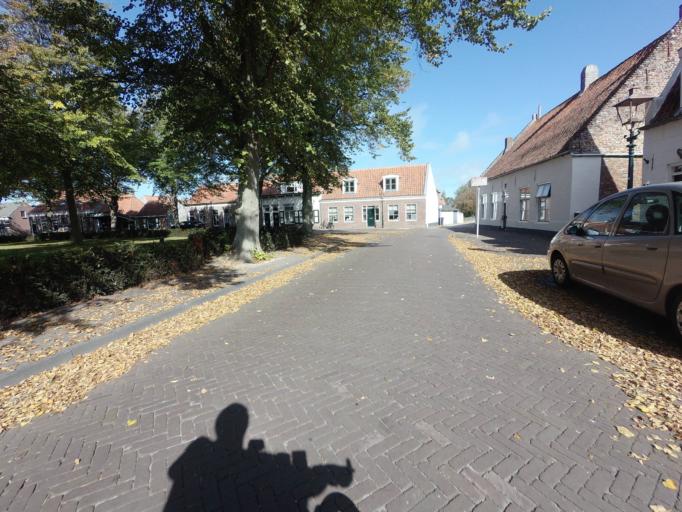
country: NL
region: Zeeland
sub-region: Gemeente Vlissingen
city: Vlissingen
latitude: 51.4993
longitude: 3.5261
